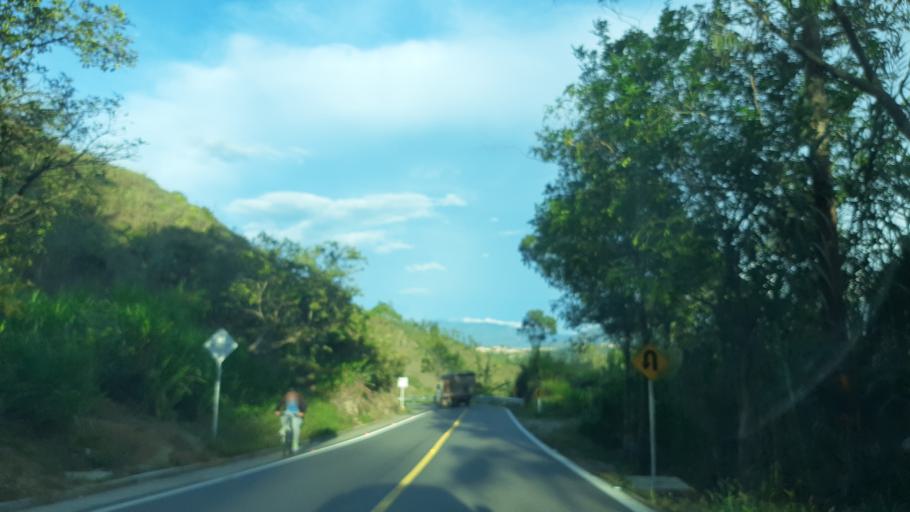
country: CO
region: Boyaca
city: Guateque
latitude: 5.0021
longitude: -73.5048
